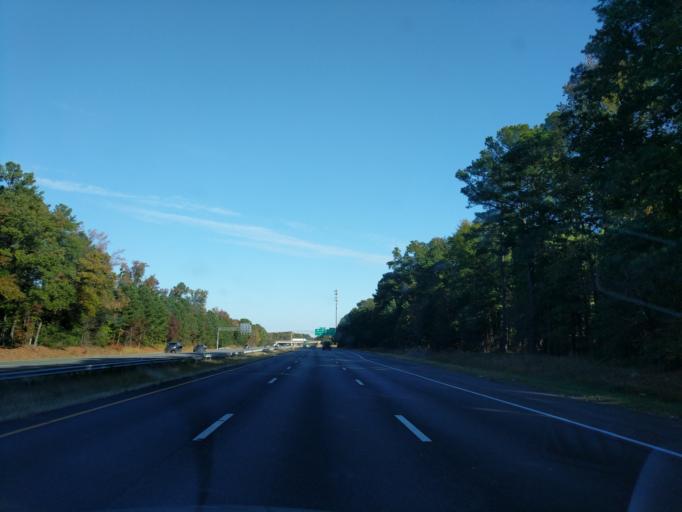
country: US
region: Virginia
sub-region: Henrico County
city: Chamberlayne
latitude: 37.6475
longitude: -77.4518
